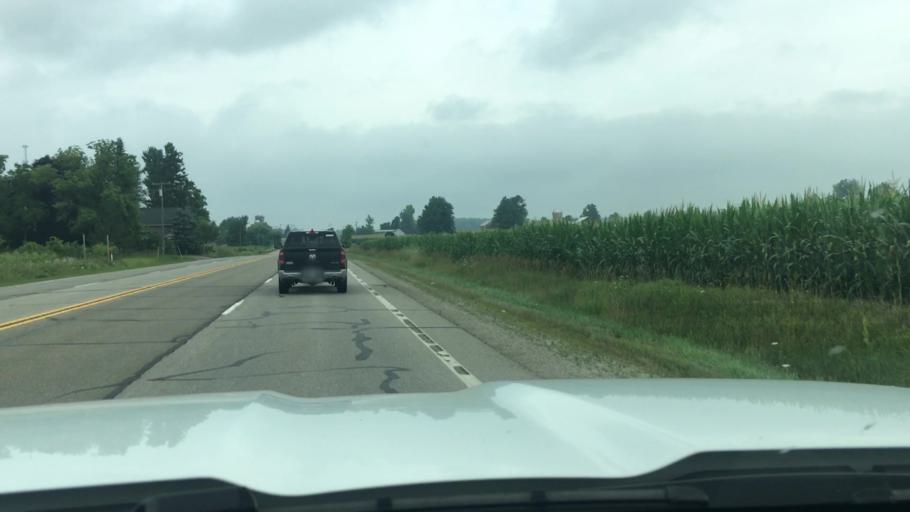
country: US
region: Michigan
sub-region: Sanilac County
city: Brown City
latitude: 43.2190
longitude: -83.0776
